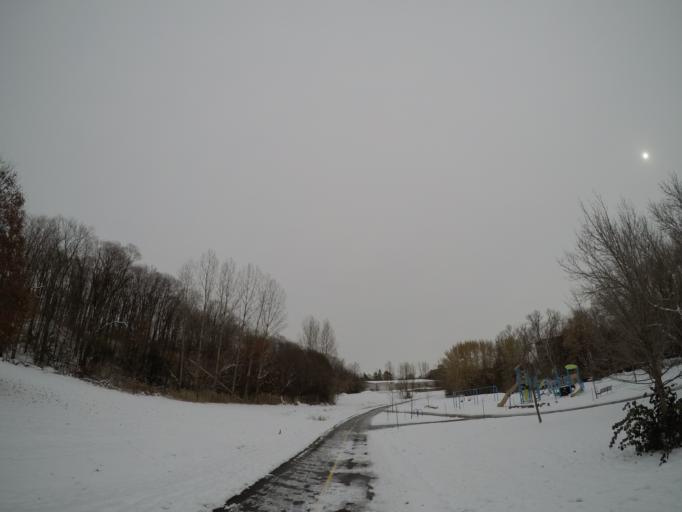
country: CA
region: Ontario
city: Waterloo
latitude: 43.4756
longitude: -80.5130
